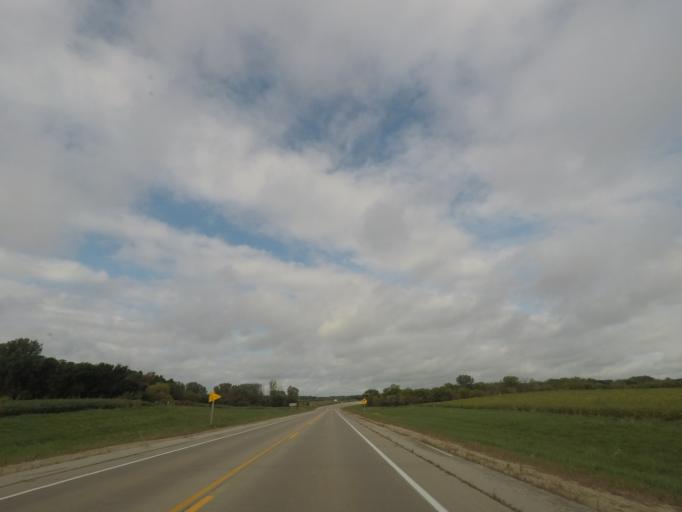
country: US
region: Wisconsin
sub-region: Dane County
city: Deerfield
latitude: 43.0209
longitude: -89.0637
